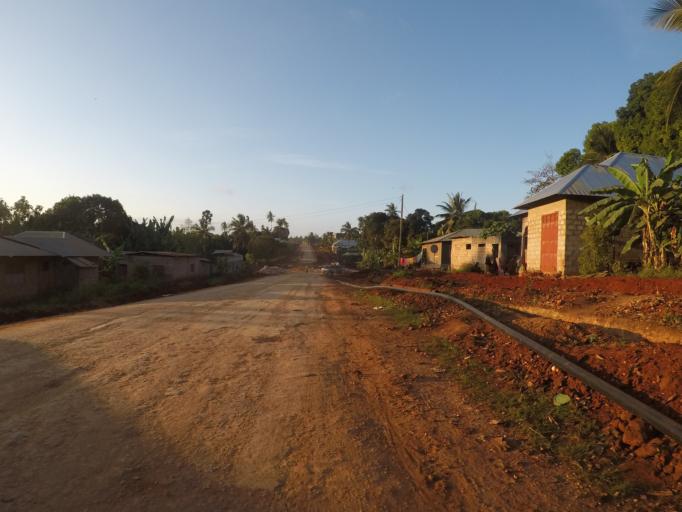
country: TZ
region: Zanzibar North
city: Gamba
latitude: -5.9163
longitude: 39.2993
